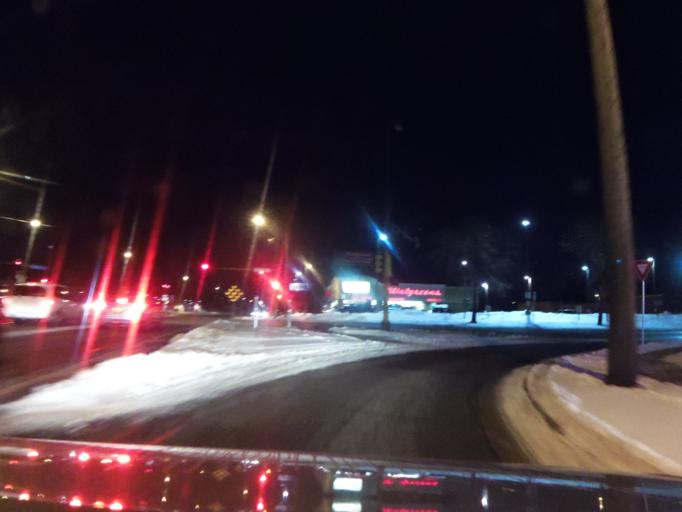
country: US
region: Minnesota
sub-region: Hennepin County
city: Richfield
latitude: 44.9194
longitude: -93.2182
